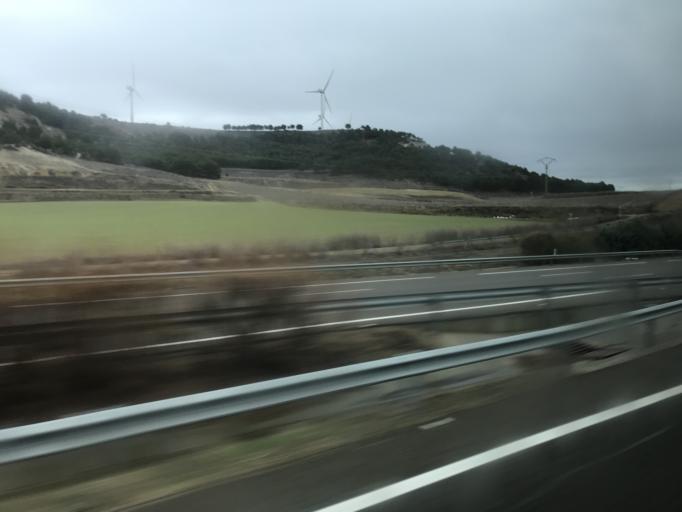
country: ES
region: Castille and Leon
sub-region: Provincia de Palencia
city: Palencia
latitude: 41.9921
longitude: -4.5029
